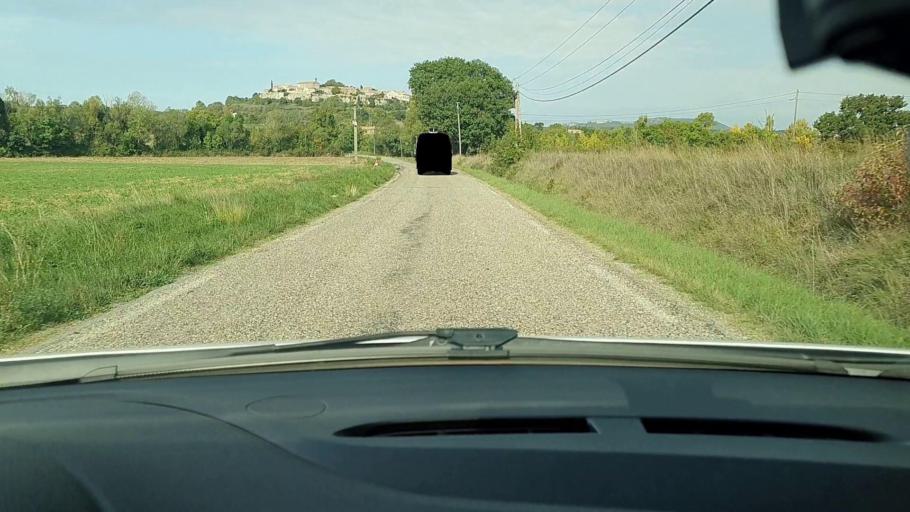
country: FR
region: Languedoc-Roussillon
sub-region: Departement du Gard
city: Goudargues
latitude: 44.1485
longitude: 4.3763
